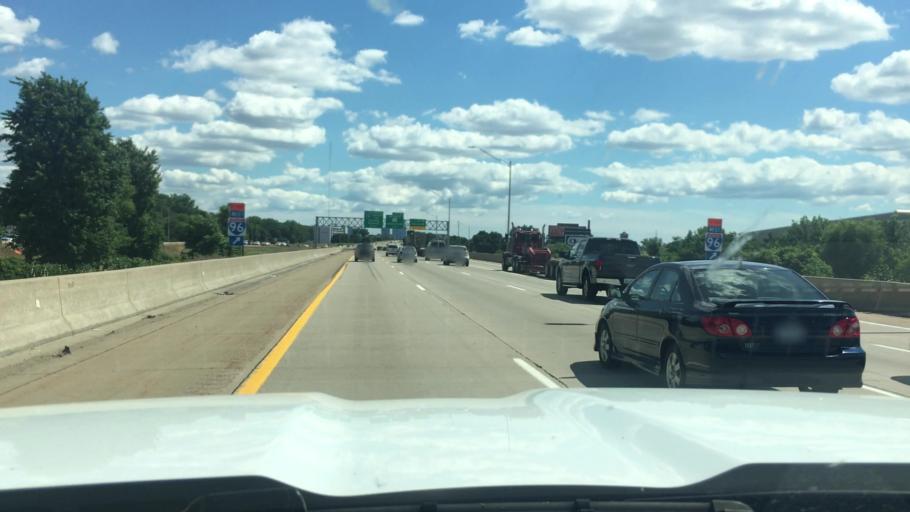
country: US
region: Michigan
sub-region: Kent County
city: Comstock Park
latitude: 43.0041
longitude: -85.6761
